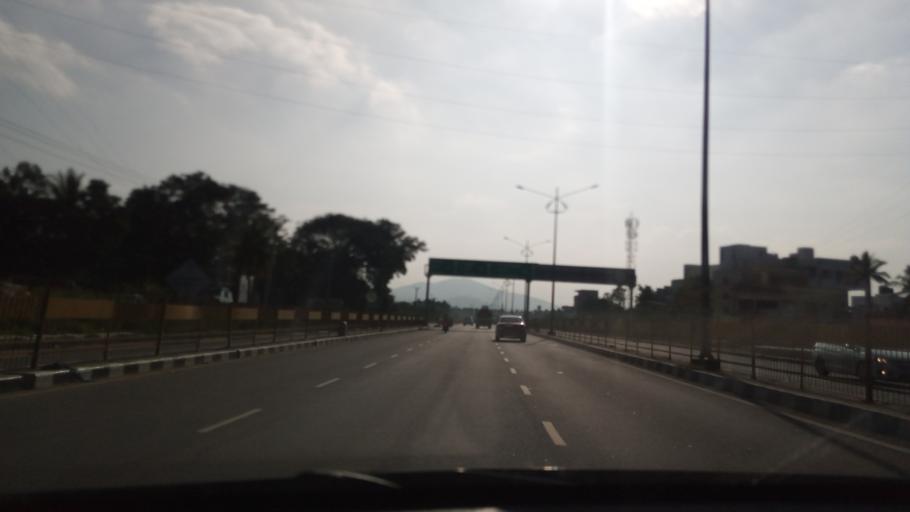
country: IN
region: Tamil Nadu
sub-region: Krishnagiri
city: Krishnagiri
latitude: 12.5288
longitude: 78.2367
